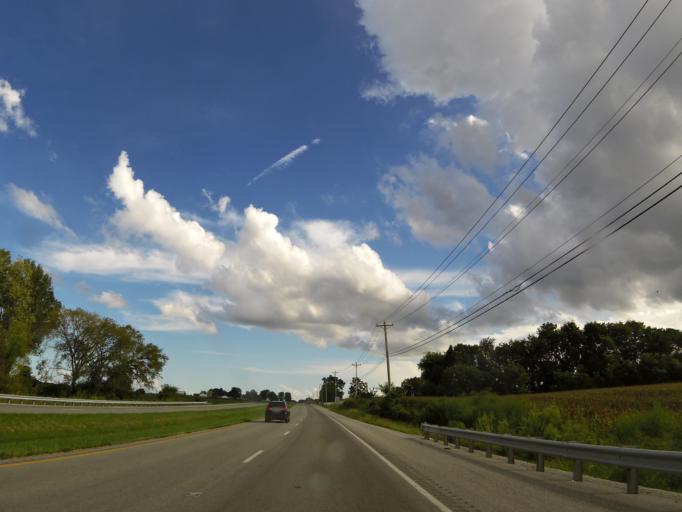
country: US
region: Kentucky
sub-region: Christian County
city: Hopkinsville
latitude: 36.7876
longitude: -87.4744
